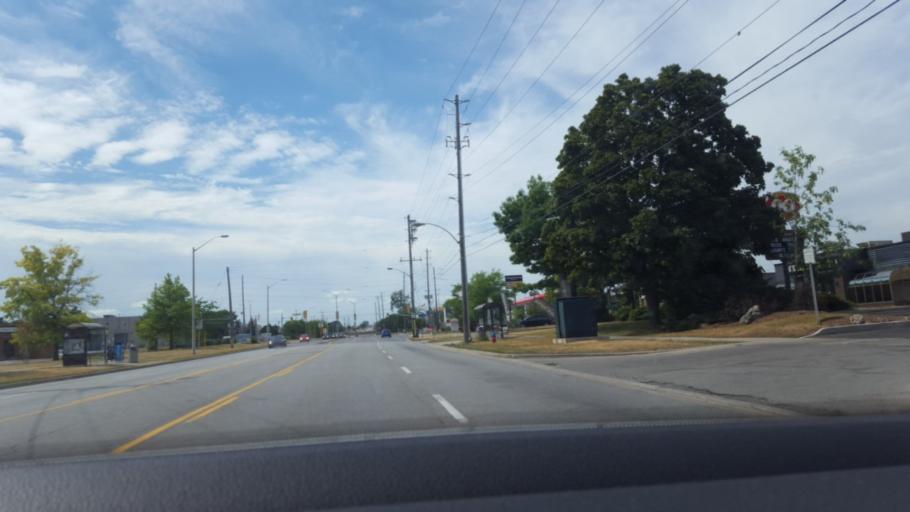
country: CA
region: Ontario
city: Burlington
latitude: 43.3725
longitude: -79.7607
